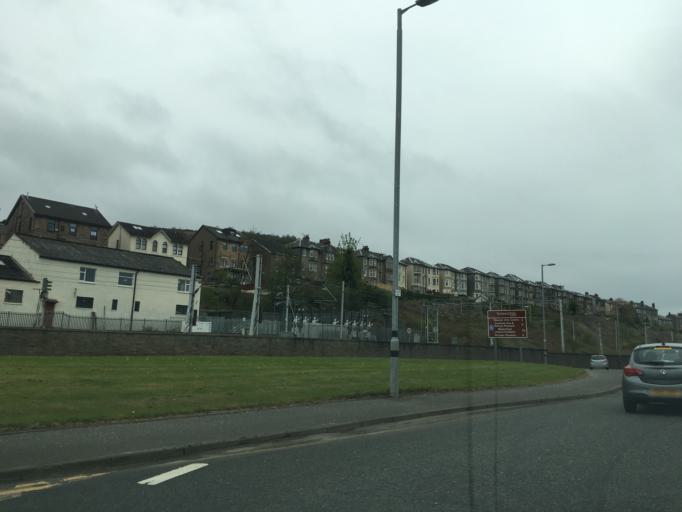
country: GB
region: Scotland
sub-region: Inverclyde
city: Port Glasgow
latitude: 55.9361
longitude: -4.7022
